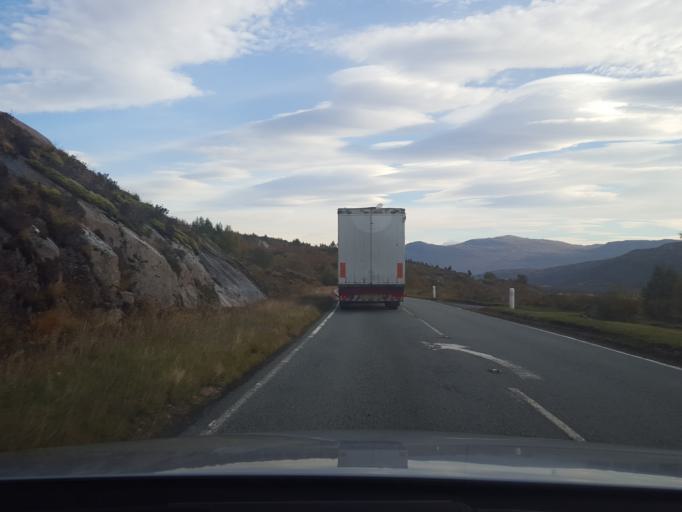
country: GB
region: Scotland
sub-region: Highland
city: Spean Bridge
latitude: 57.1496
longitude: -5.0338
